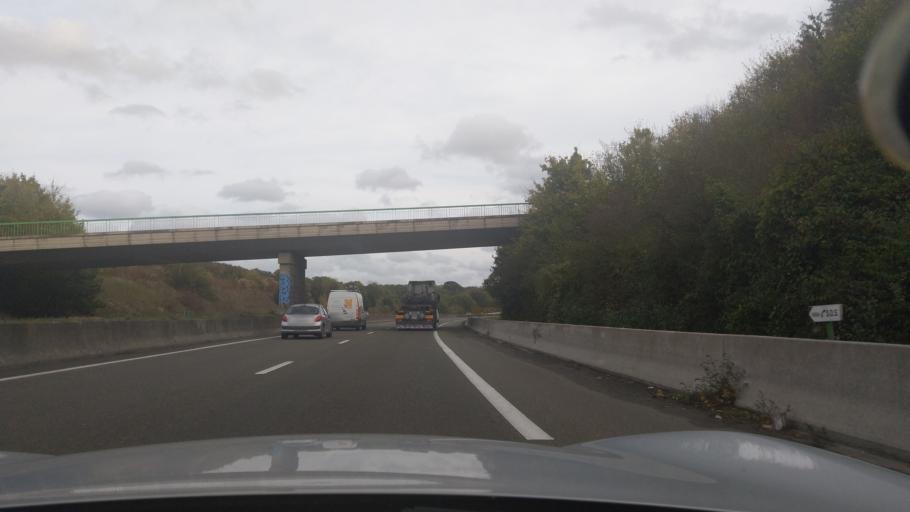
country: FR
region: Ile-de-France
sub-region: Departement du Val-d'Oise
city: Meriel
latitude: 49.0725
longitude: 2.2420
